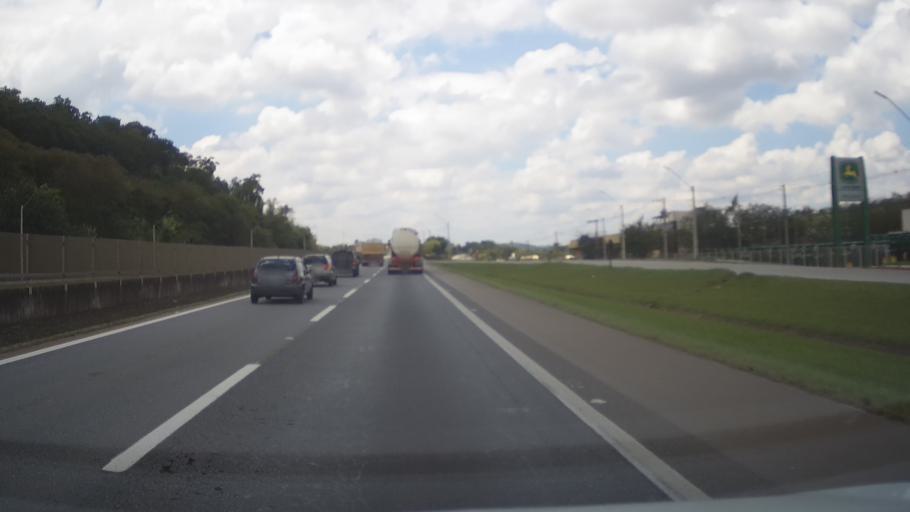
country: BR
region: Minas Gerais
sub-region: Tres Coracoes
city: Tres Coracoes
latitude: -21.6665
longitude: -45.3131
